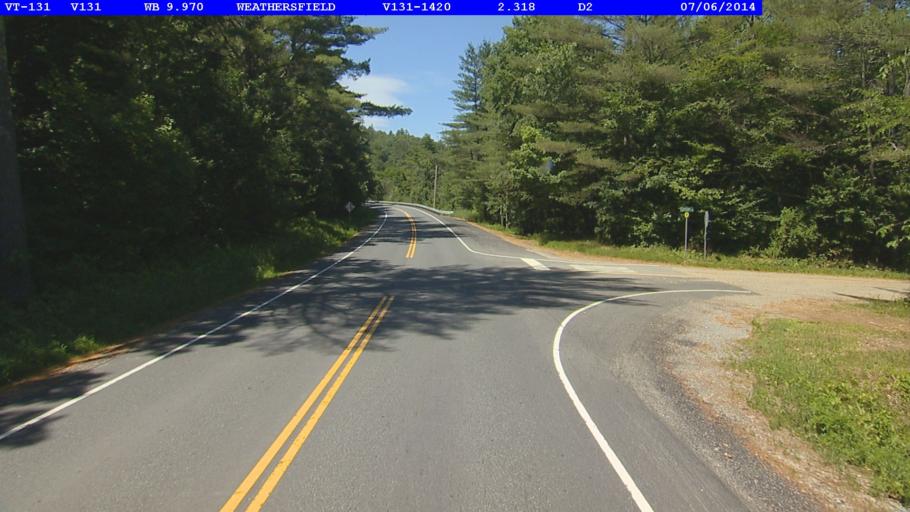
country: US
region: Vermont
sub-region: Windsor County
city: Springfield
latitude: 43.4086
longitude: -72.5027
